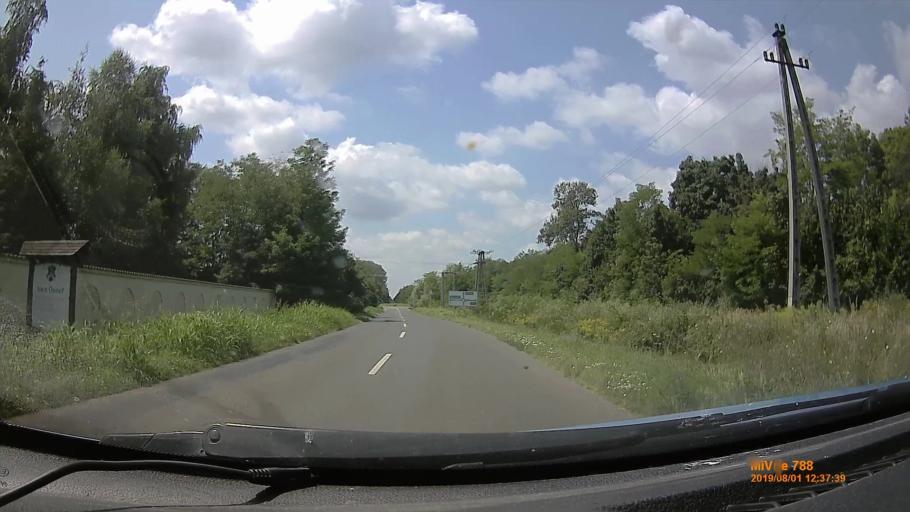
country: HU
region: Baranya
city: Harkany
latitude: 45.8453
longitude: 18.2251
